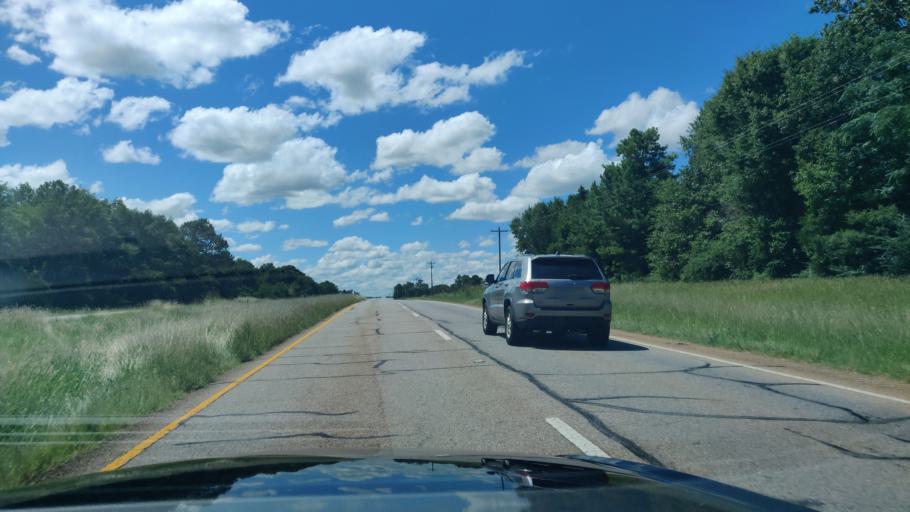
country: US
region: Georgia
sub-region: Webster County
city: Preston
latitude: 31.9265
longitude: -84.5544
